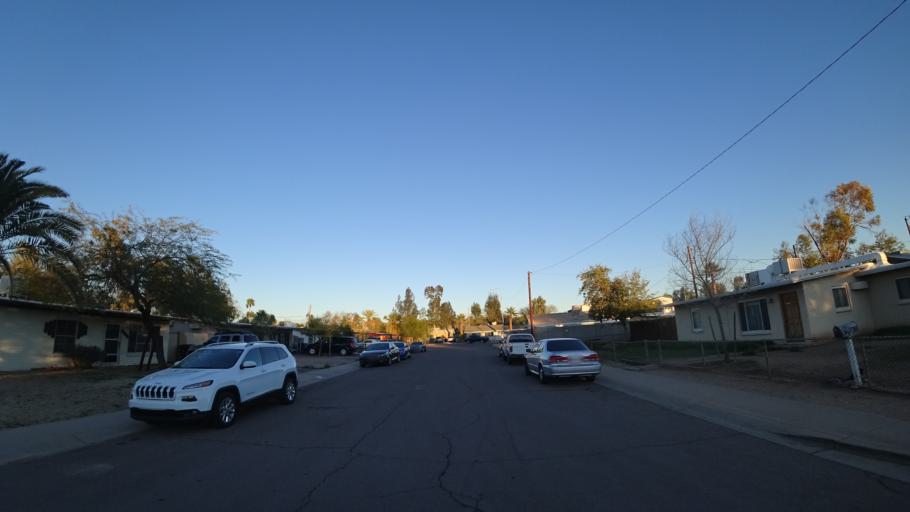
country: US
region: Arizona
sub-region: Maricopa County
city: Tempe Junction
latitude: 33.4279
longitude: -111.9558
